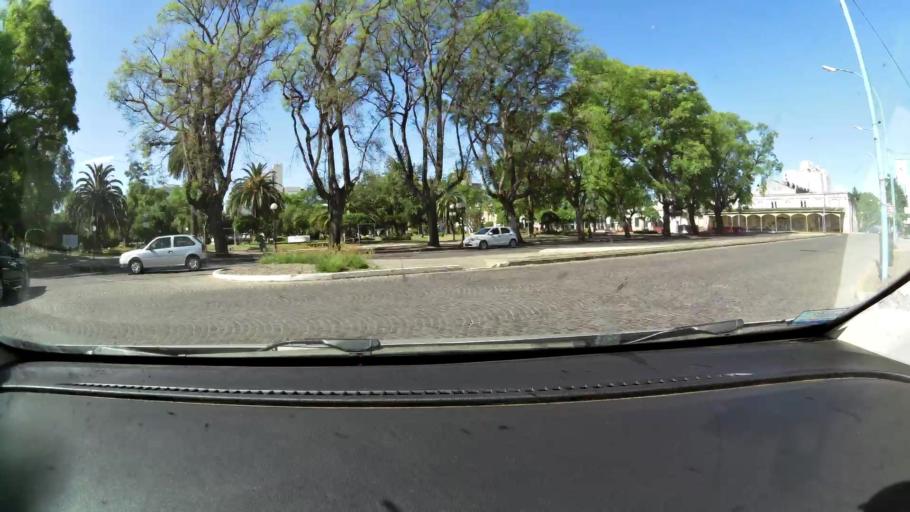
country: AR
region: Santa Fe
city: Rafaela
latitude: -31.2536
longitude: -61.4918
